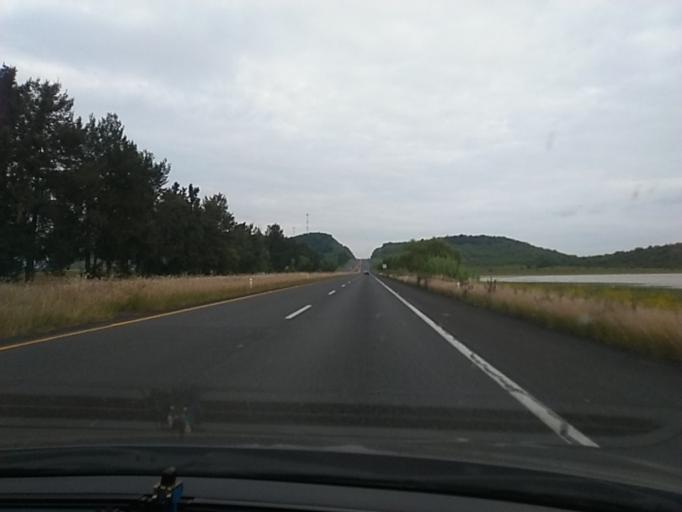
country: MX
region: Michoacan
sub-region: Puruandiro
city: San Lorenzo
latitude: 19.9467
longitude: -101.6391
